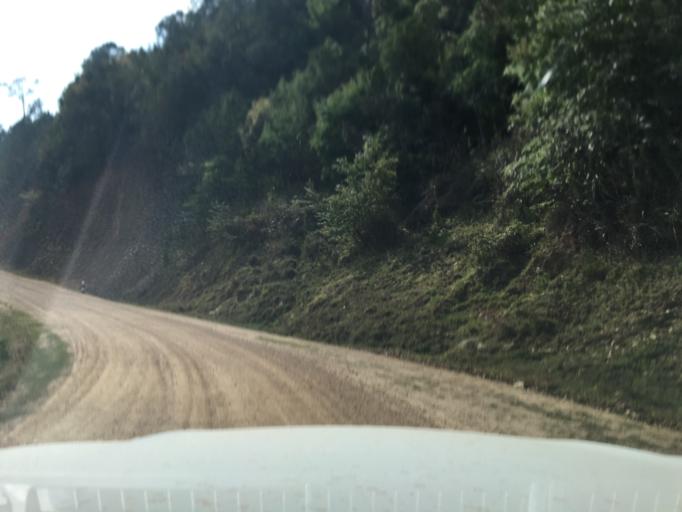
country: LA
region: Houaphan
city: Huameung
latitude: 20.2036
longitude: 103.8438
